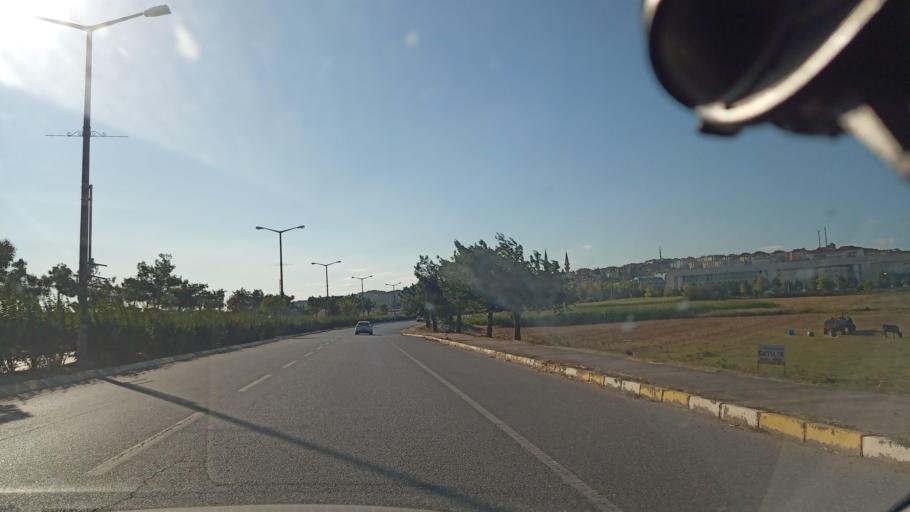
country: TR
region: Sakarya
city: Kazimpasa
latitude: 40.8494
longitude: 30.3209
